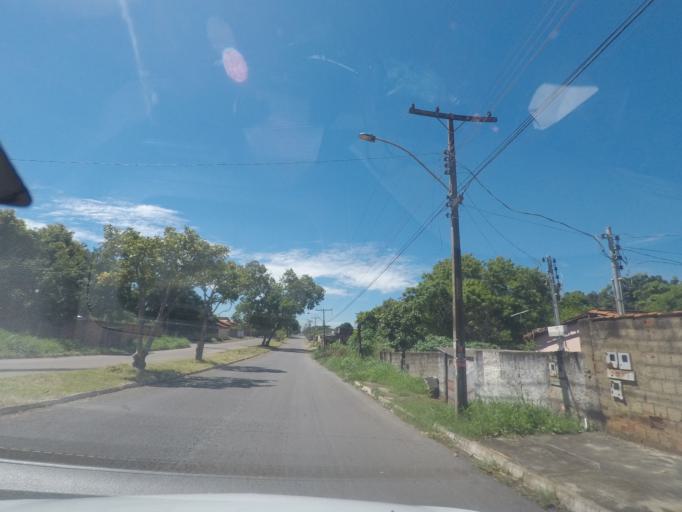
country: BR
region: Goias
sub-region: Aparecida De Goiania
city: Aparecida de Goiania
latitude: -16.7772
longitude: -49.3392
